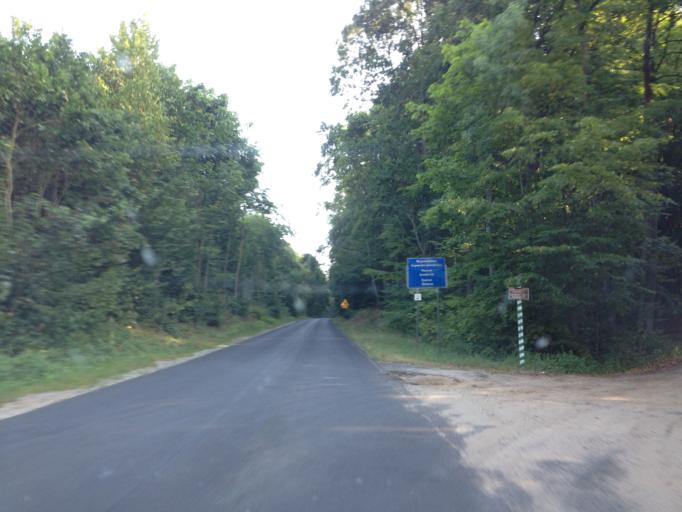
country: PL
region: Warmian-Masurian Voivodeship
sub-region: Powiat nowomiejski
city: Biskupiec
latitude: 53.4084
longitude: 19.3433
